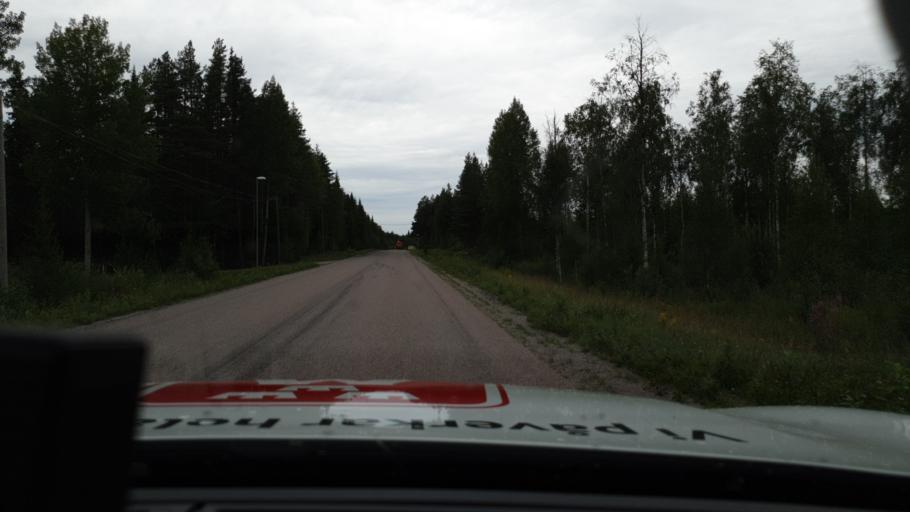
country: SE
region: Norrbotten
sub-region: Bodens Kommun
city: Saevast
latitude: 65.8827
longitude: 21.8574
